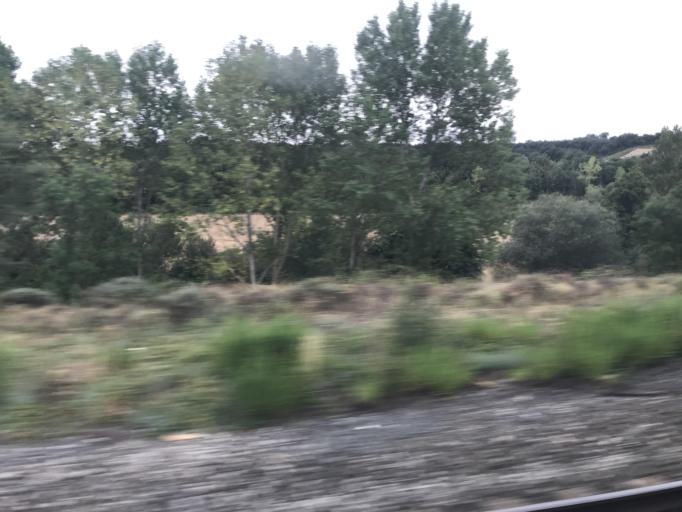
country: ES
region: Basque Country
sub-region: Provincia de Alava
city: Arminon
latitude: 42.7461
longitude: -2.8633
